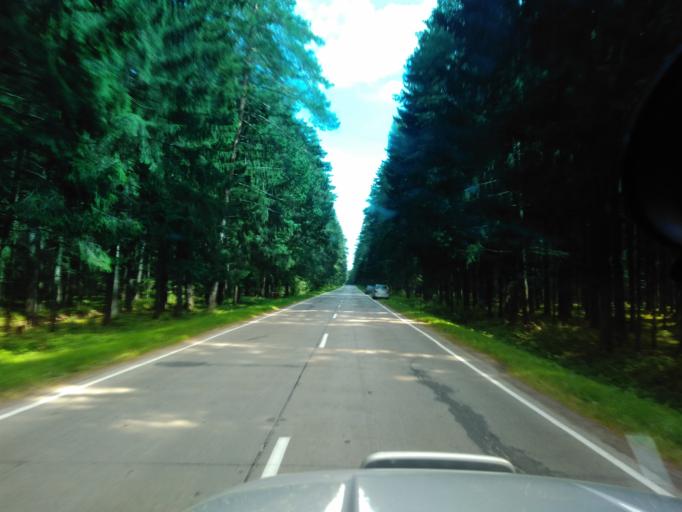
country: BY
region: Minsk
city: Stan'kava
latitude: 53.6227
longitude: 27.2971
